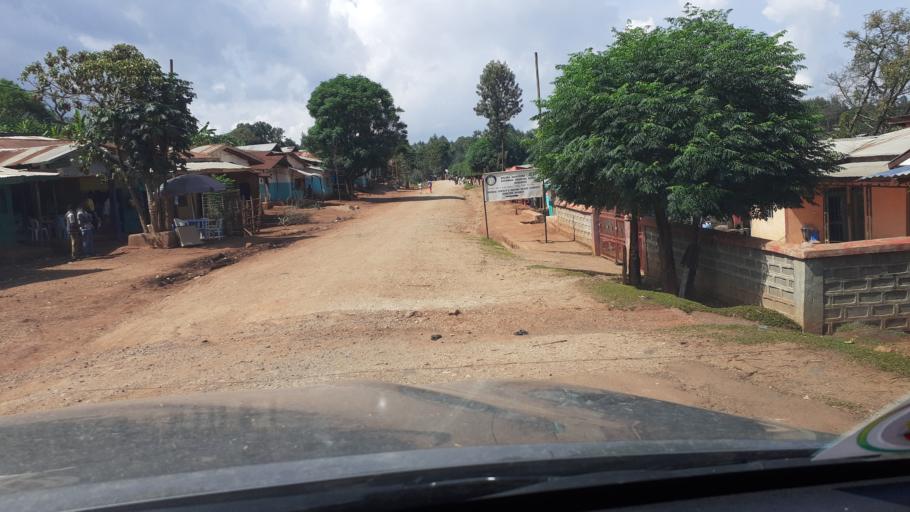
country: ET
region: Oromiya
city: Gimbi
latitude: 9.2744
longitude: 35.6887
